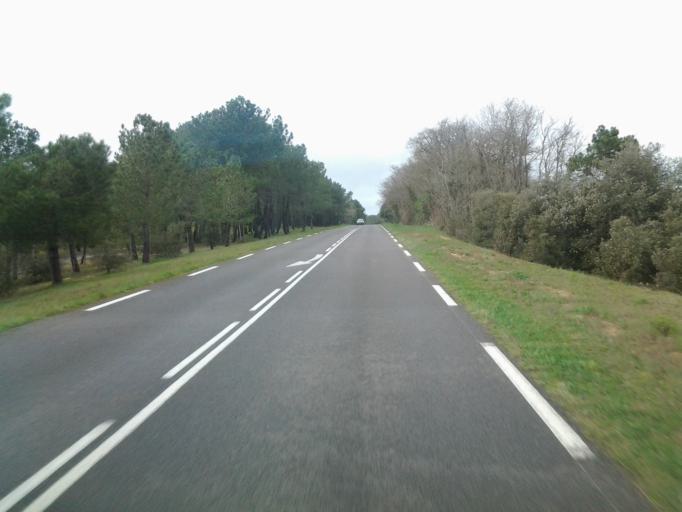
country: FR
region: Pays de la Loire
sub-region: Departement de la Vendee
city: La Tranche-sur-Mer
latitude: 46.3688
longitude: -1.4591
